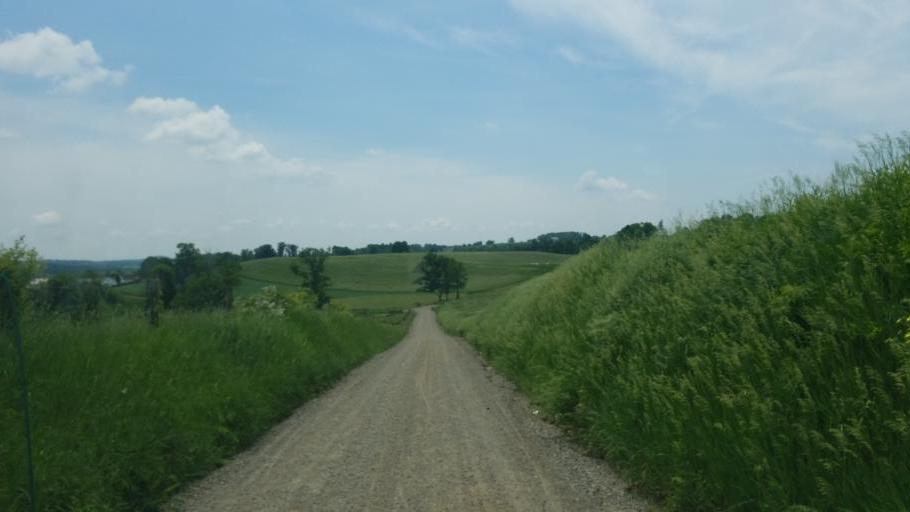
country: US
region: Ohio
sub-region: Holmes County
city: Millersburg
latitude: 40.4751
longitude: -81.7963
